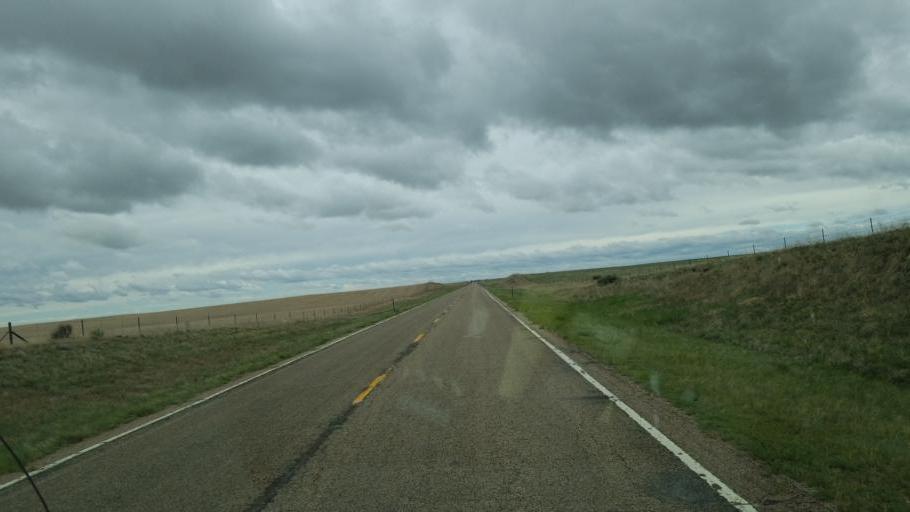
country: US
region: Colorado
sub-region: Lincoln County
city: Hugo
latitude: 38.8515
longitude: -103.6445
